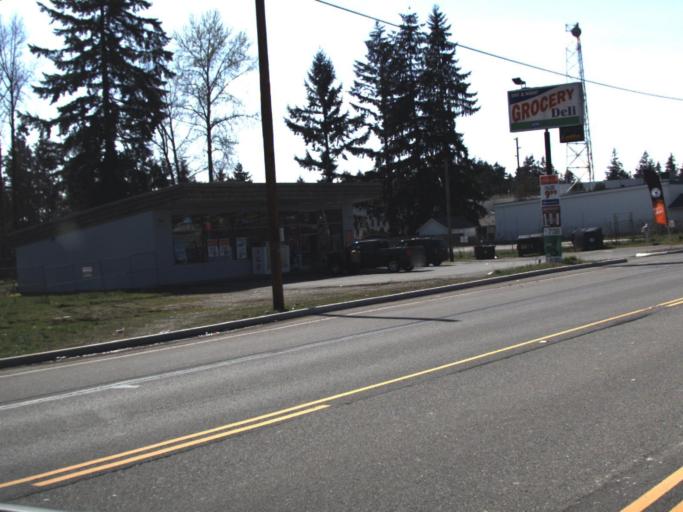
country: US
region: Washington
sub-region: King County
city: Lea Hill
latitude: 47.2883
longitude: -122.1848
